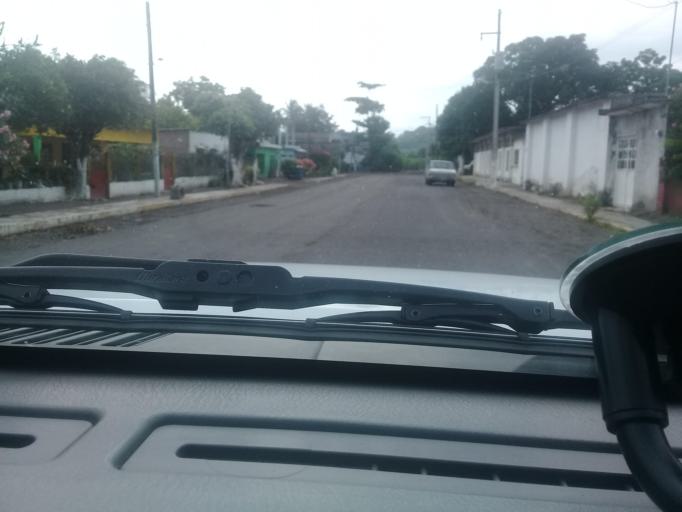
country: MX
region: Veracruz
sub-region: Paso de Ovejas
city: Tolome
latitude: 19.2629
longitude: -96.4101
